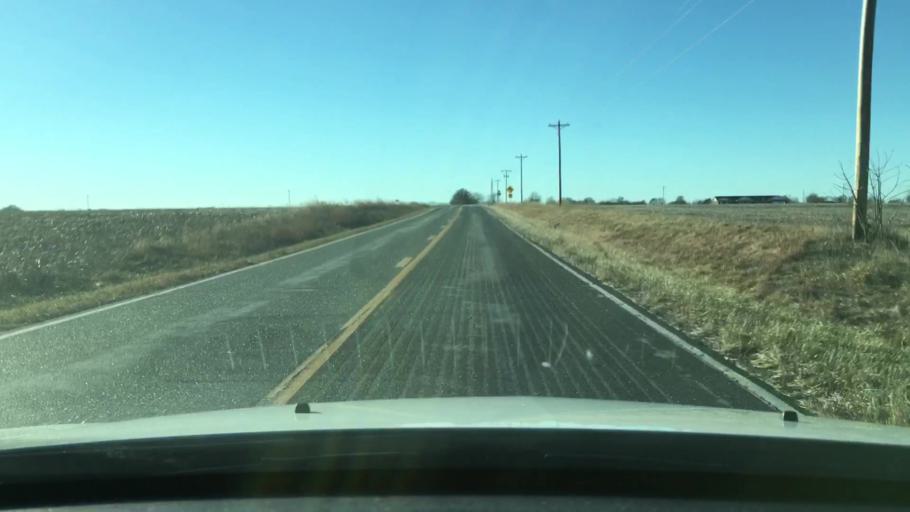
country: US
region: Missouri
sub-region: Audrain County
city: Mexico
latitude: 39.2761
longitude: -91.8096
